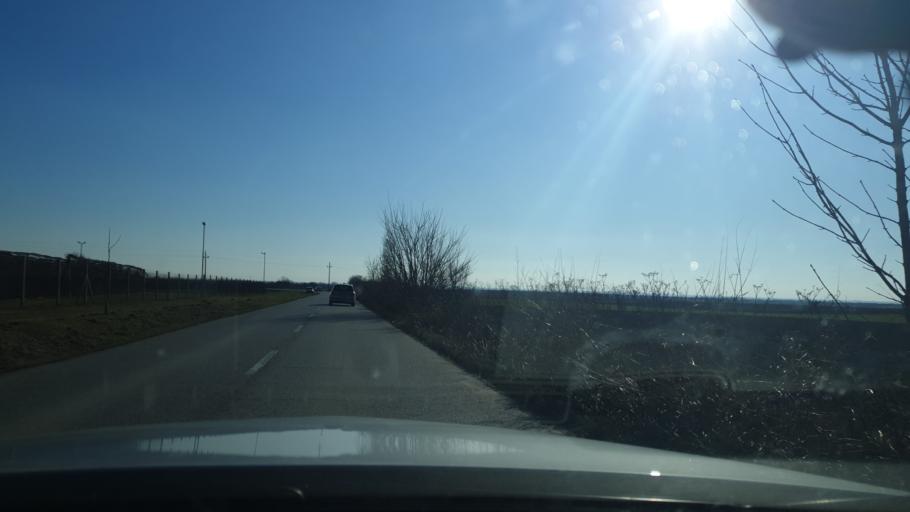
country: RS
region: Autonomna Pokrajina Vojvodina
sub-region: Sremski Okrug
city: Ruma
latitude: 45.0449
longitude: 19.8050
